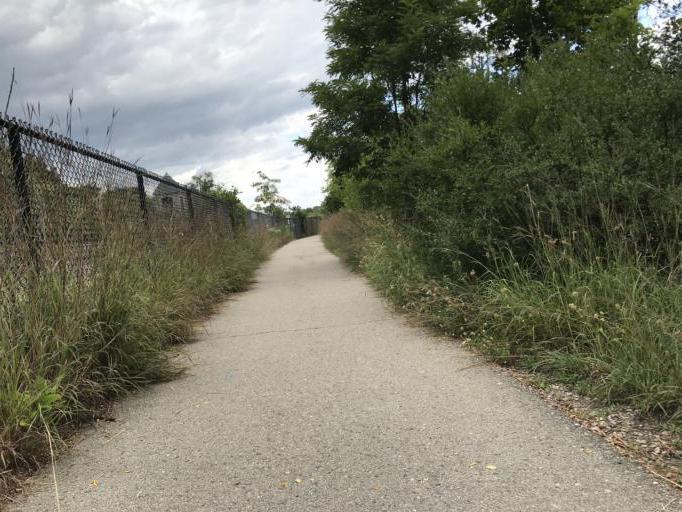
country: US
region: Michigan
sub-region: Washtenaw County
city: Ann Arbor
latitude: 42.2919
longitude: -83.7466
